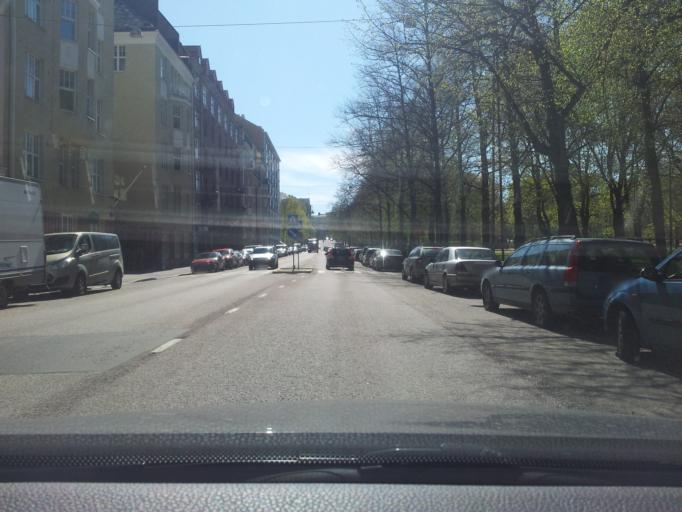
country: FI
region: Uusimaa
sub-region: Helsinki
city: Helsinki
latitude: 60.1830
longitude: 24.9191
